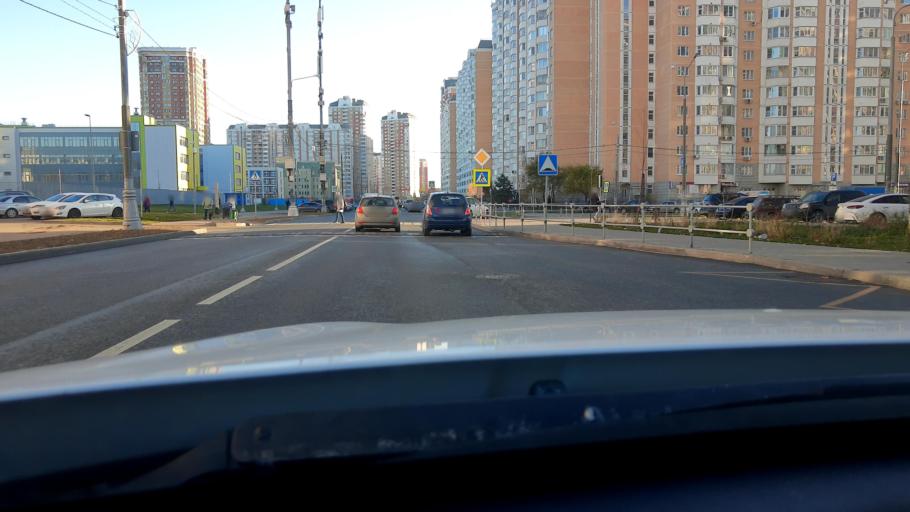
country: RU
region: Moskovskaya
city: Moskovskiy
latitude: 55.5940
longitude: 37.3678
